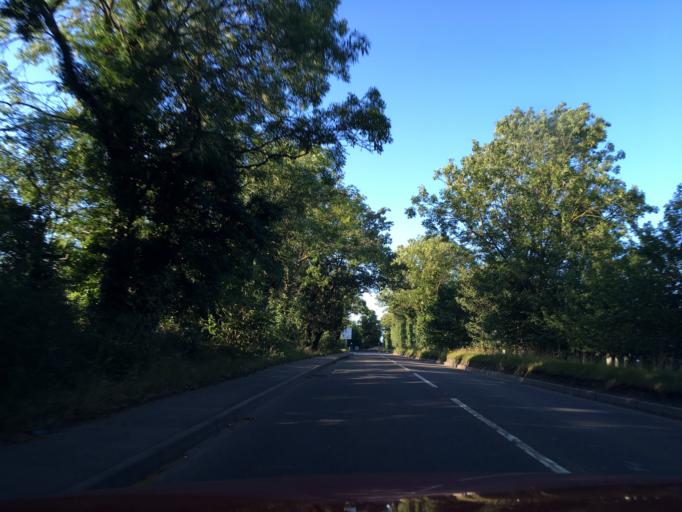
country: GB
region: England
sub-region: Hampshire
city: Tadley
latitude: 51.3682
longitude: -1.1526
